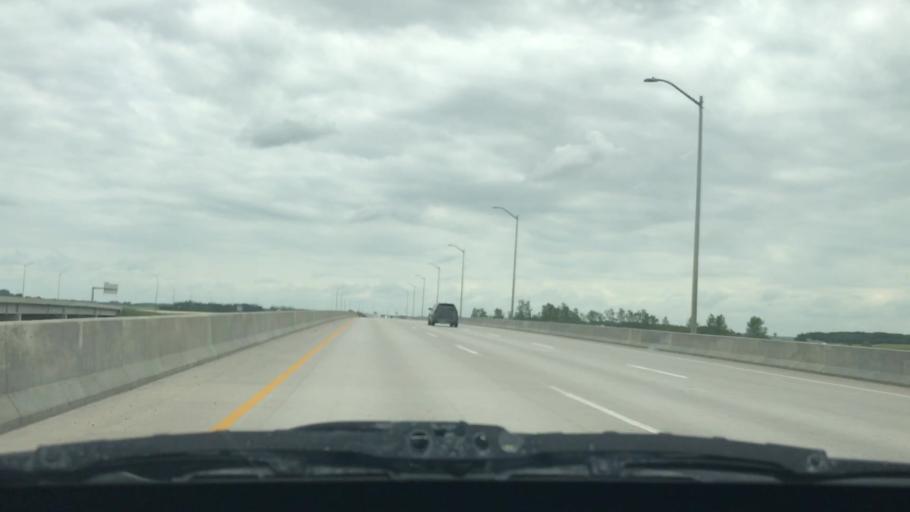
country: CA
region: Manitoba
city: Winnipeg
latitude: 49.8319
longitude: -96.9573
